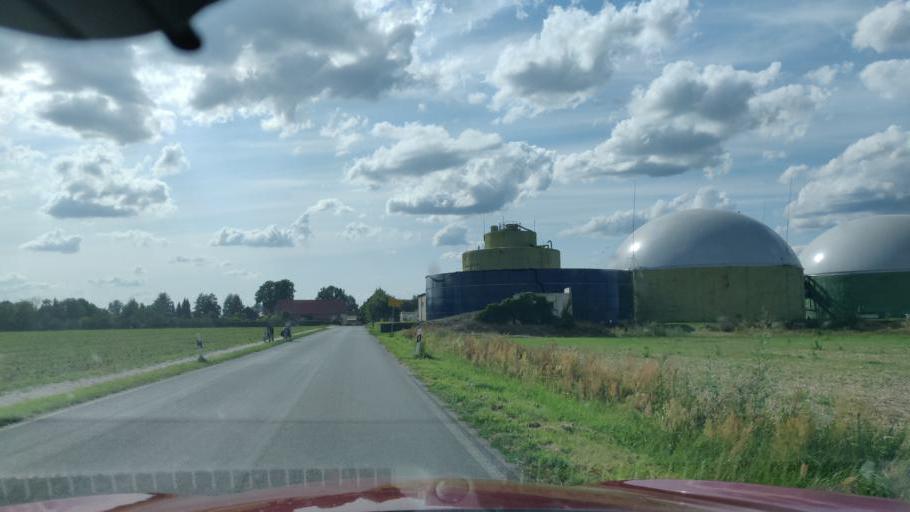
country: DE
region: Saxony
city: Schildau
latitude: 51.4821
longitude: 12.9108
